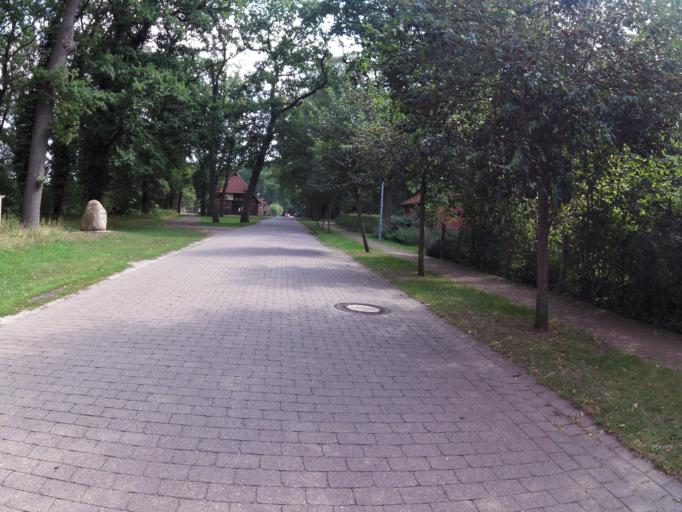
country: DE
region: Lower Saxony
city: Estorf
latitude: 52.5880
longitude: 9.1432
